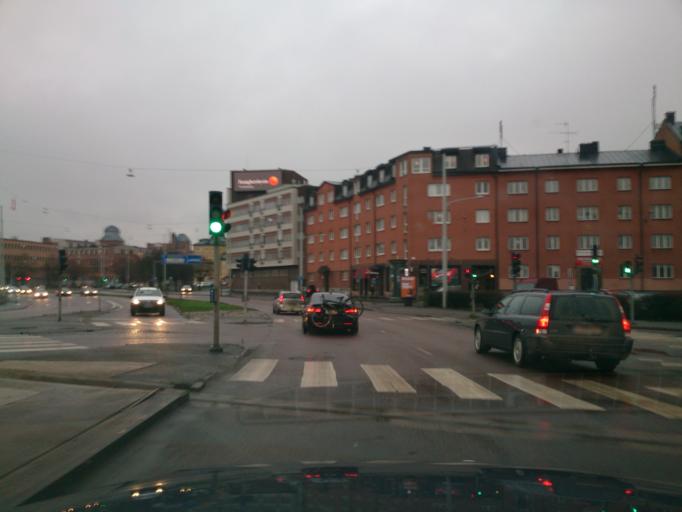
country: SE
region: OEstergoetland
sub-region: Norrkopings Kommun
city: Norrkoping
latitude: 58.5940
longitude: 16.1943
